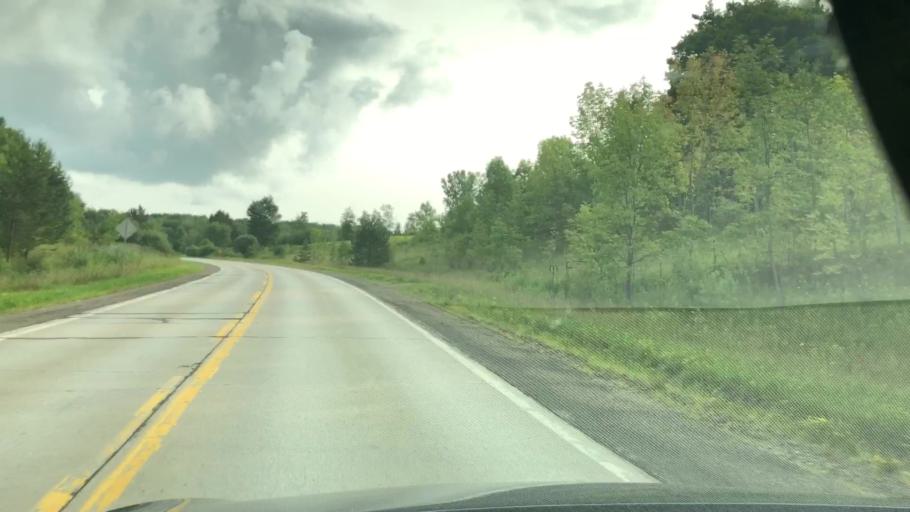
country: US
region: Pennsylvania
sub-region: Erie County
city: Union City
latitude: 41.9627
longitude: -79.8527
